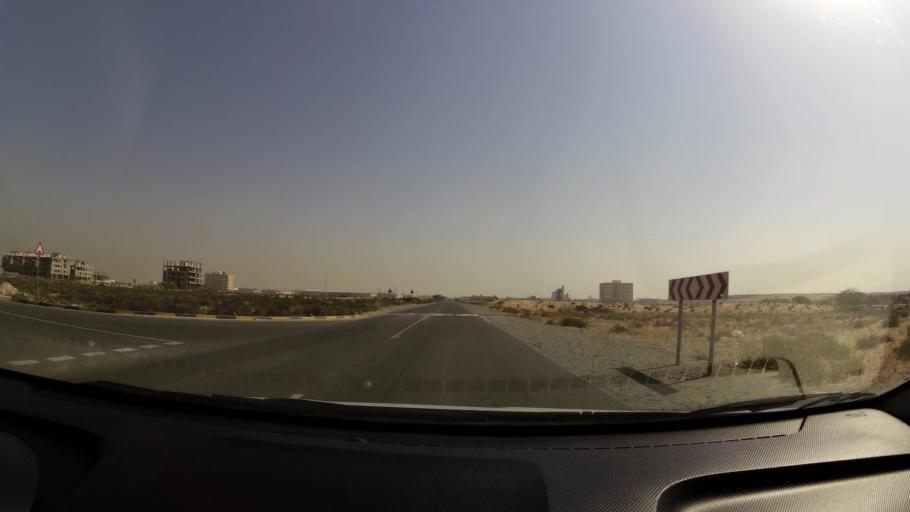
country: AE
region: Ajman
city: Ajman
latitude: 25.4239
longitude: 55.5399
